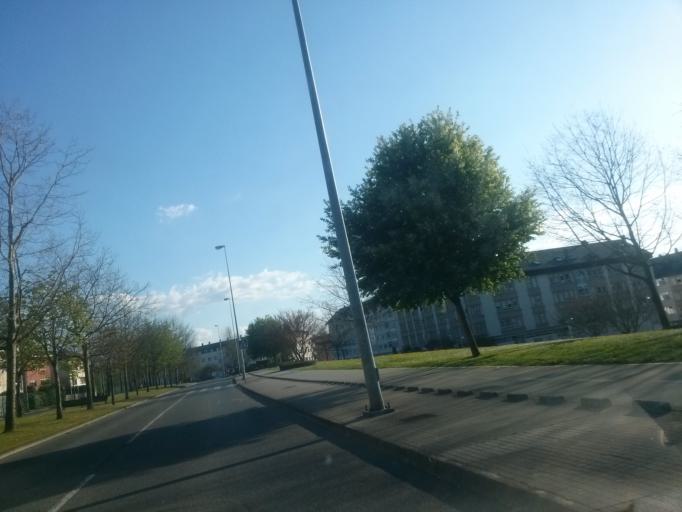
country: ES
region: Galicia
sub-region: Provincia de Lugo
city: Lugo
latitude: 42.9991
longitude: -7.5547
